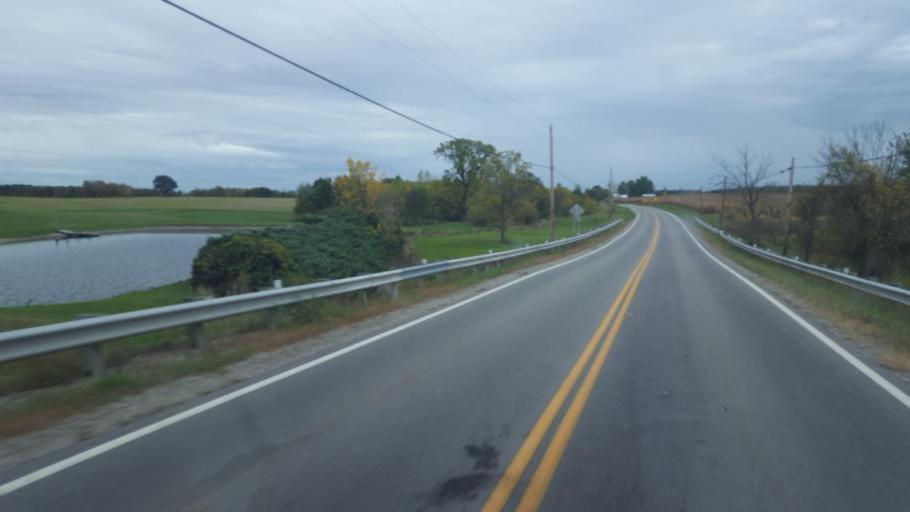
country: US
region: Ohio
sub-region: Huron County
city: New London
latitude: 41.1211
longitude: -82.4092
